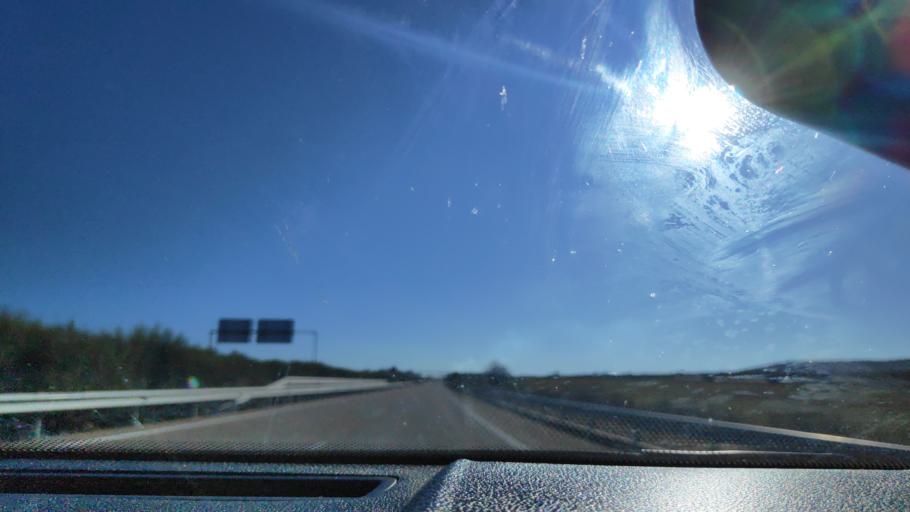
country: ES
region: Extremadura
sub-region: Provincia de Badajoz
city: Villafranca de los Barros
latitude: 38.5217
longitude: -6.3500
